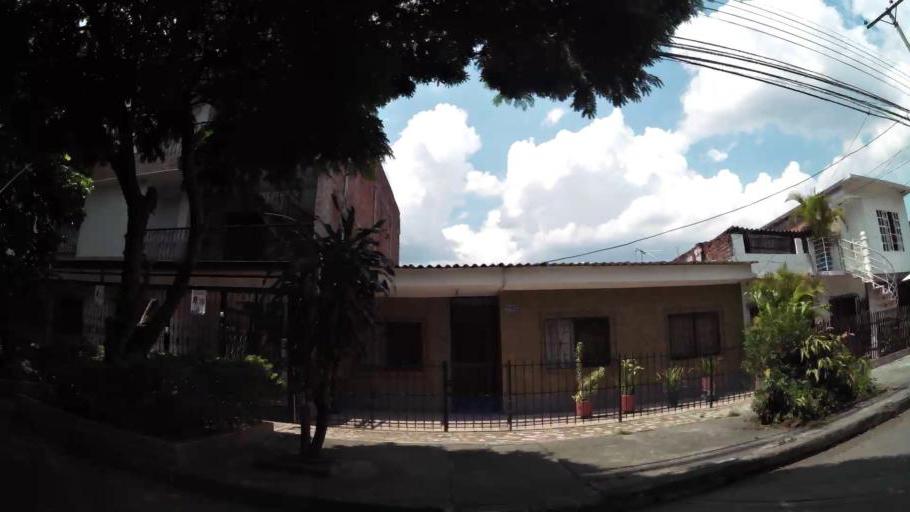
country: CO
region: Valle del Cauca
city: Cali
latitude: 3.4656
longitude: -76.5060
